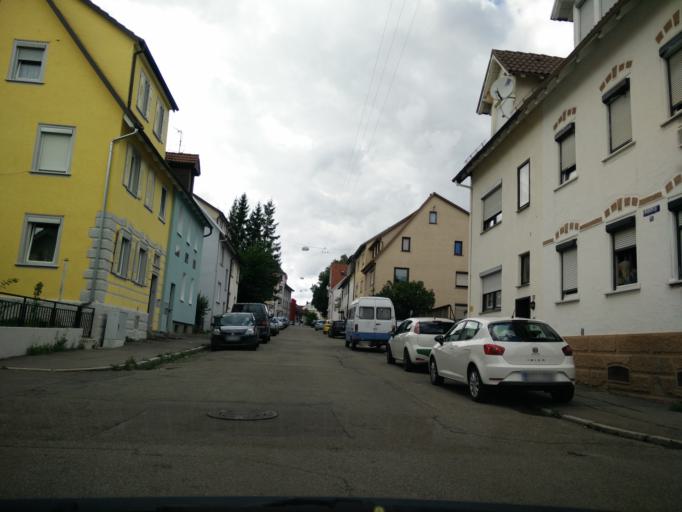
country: DE
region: Baden-Wuerttemberg
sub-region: Freiburg Region
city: Dauchingen
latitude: 48.0596
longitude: 8.5304
